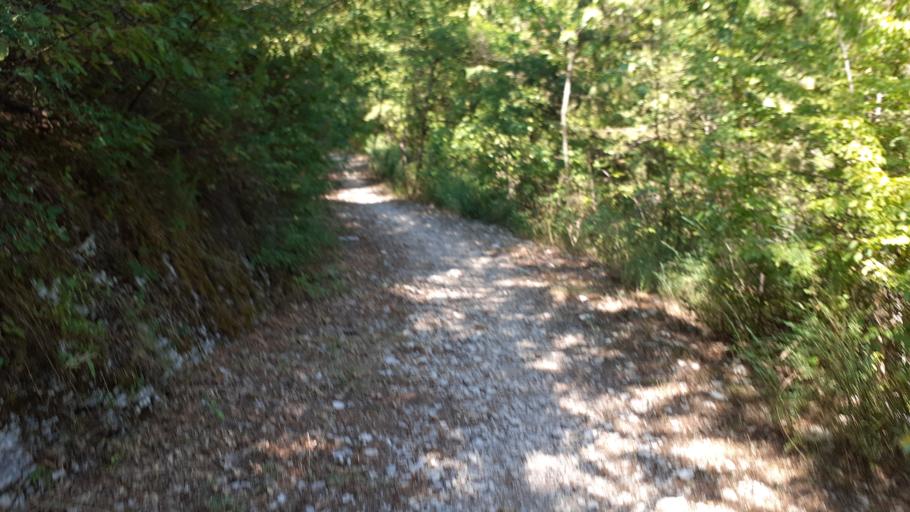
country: IT
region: Abruzzo
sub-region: Provincia di Pescara
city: San Valentino in Abruzzo Citeriore
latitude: 42.2429
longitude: 13.9699
